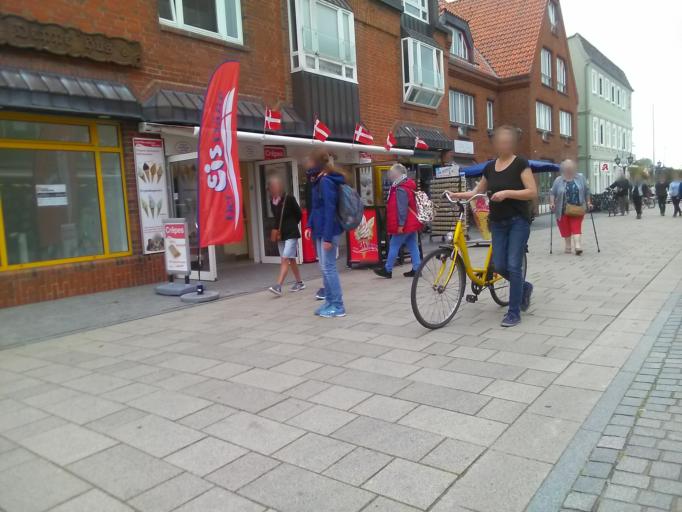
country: DE
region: Schleswig-Holstein
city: Wyk auf Fohr
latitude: 54.6901
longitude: 8.5715
